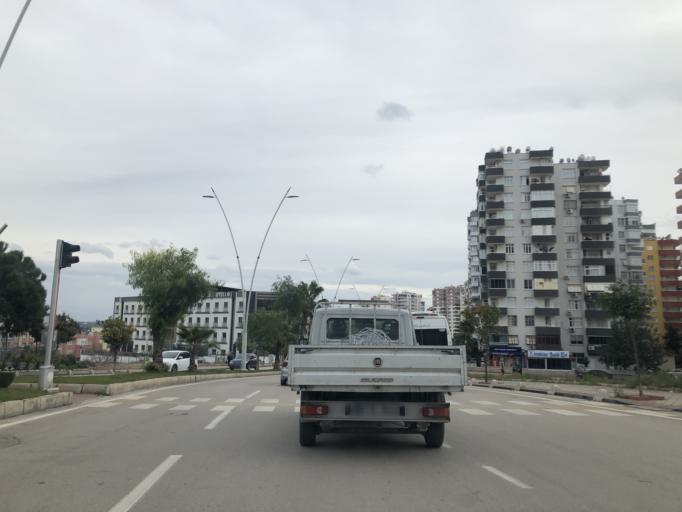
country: TR
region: Adana
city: Adana
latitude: 37.0542
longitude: 35.2883
